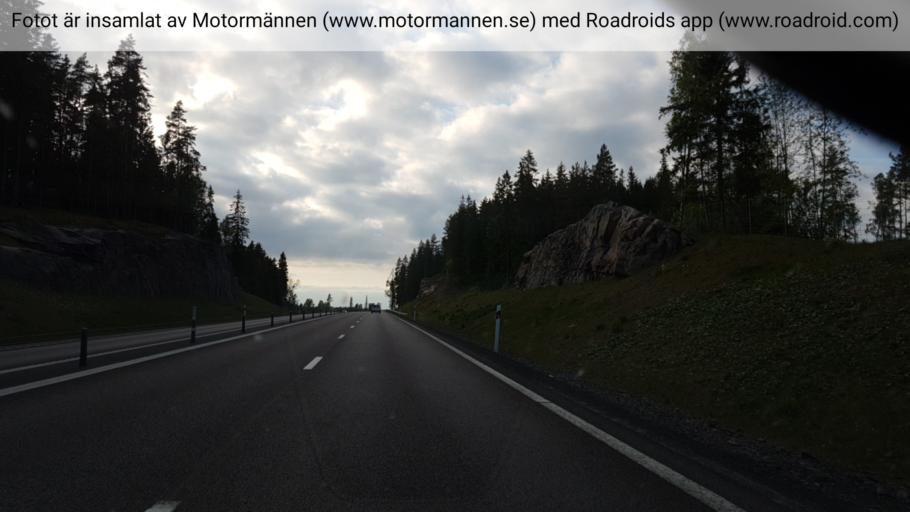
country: SE
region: Joenkoeping
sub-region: Jonkopings Kommun
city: Tenhult
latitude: 57.7254
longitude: 14.3502
